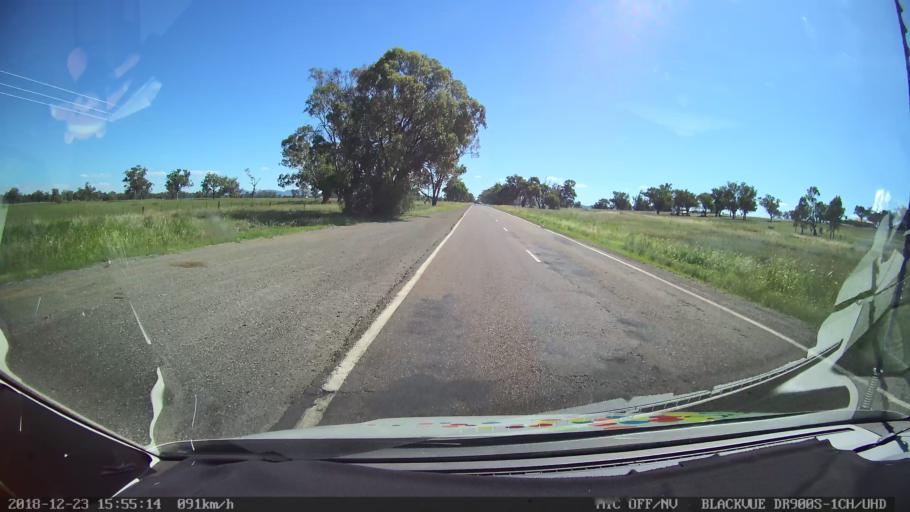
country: AU
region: New South Wales
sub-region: Tamworth Municipality
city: Phillip
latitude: -31.1533
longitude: 150.8705
